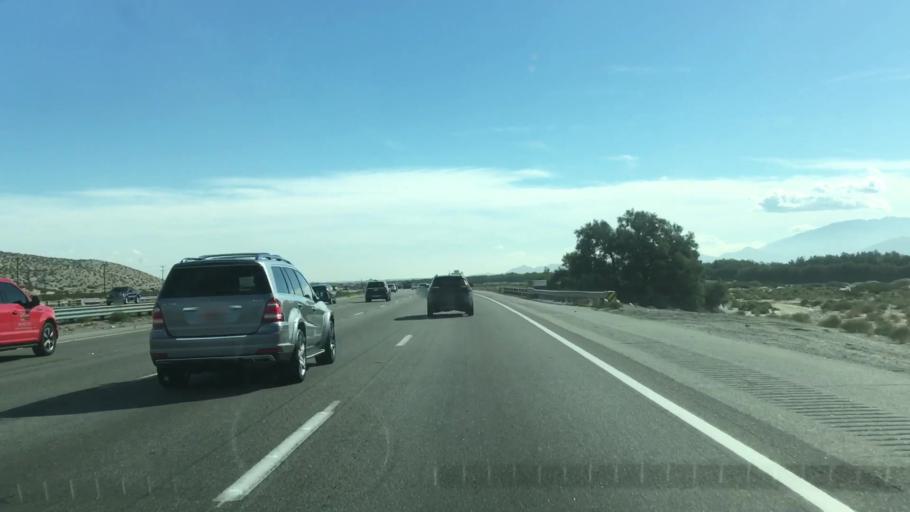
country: US
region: California
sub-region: Riverside County
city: Garnet
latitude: 33.8697
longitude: -116.4930
